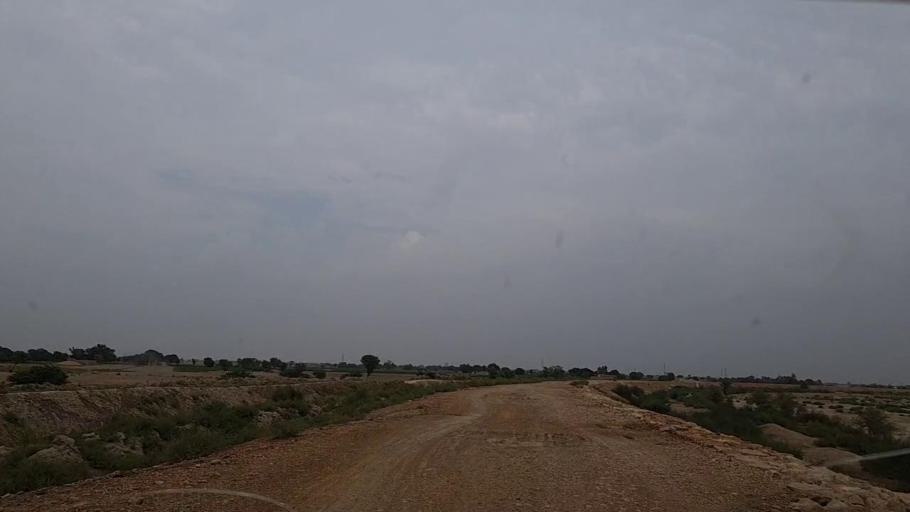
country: PK
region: Sindh
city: Johi
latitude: 26.7042
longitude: 67.5947
